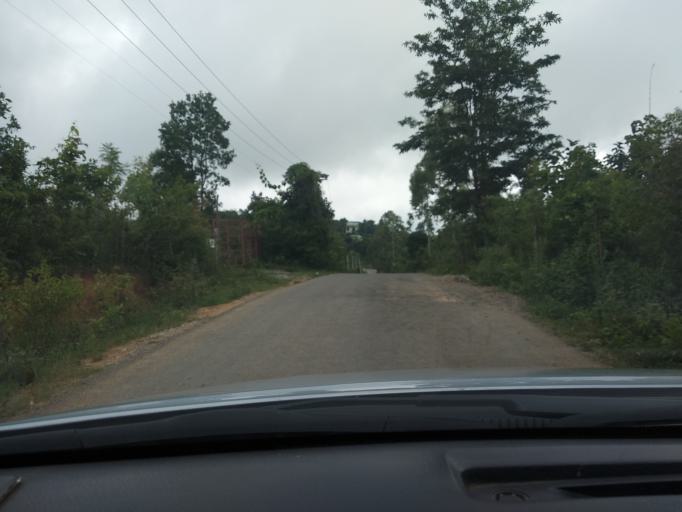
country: MM
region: Mandalay
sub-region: Pyin Oo Lwin District
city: Pyin Oo Lwin
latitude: 21.9160
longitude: 96.3836
